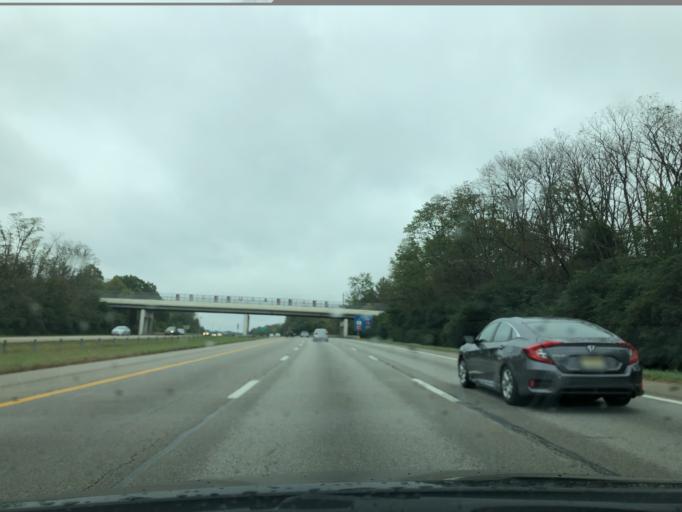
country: US
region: Ohio
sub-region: Hamilton County
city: The Village of Indian Hill
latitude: 39.2347
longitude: -84.2935
